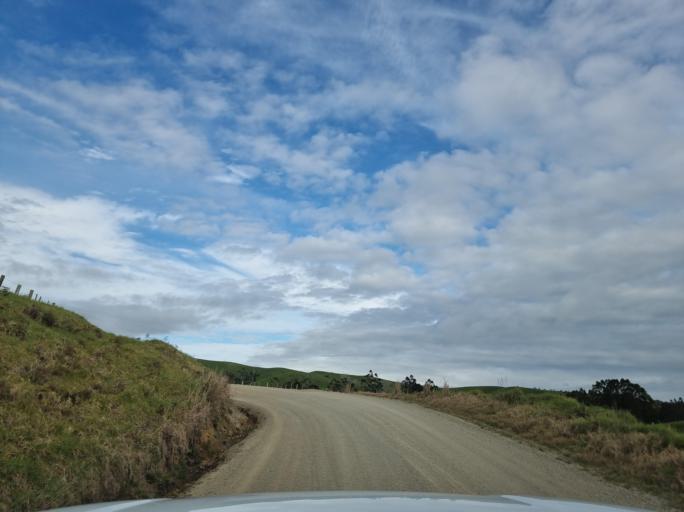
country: NZ
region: Northland
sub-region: Whangarei
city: Ruakaka
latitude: -36.0789
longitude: 174.3712
